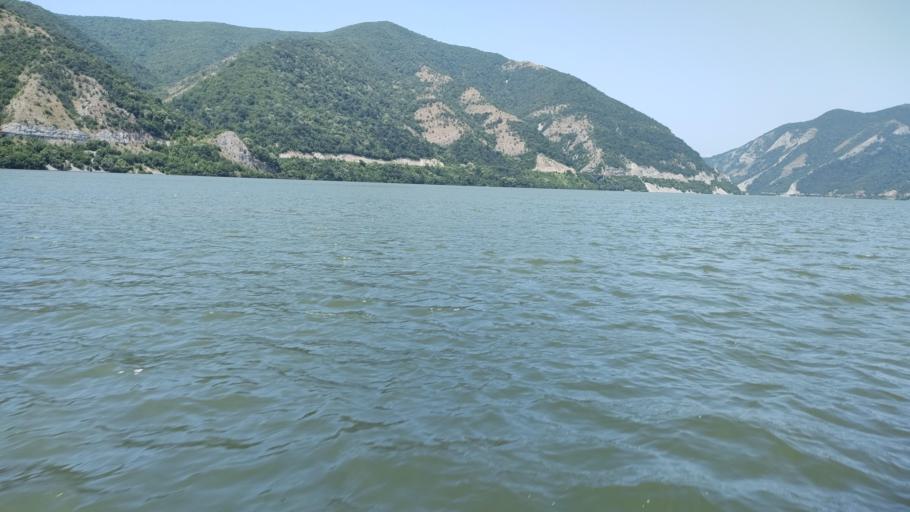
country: RO
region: Mehedinti
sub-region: Comuna Svinita
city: Svinita
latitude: 44.5674
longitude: 22.0299
